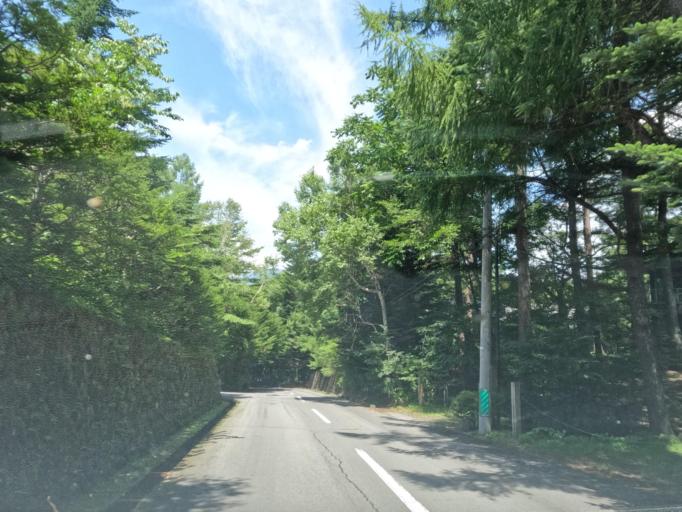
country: JP
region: Nagano
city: Komoro
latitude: 36.3593
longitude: 138.5979
